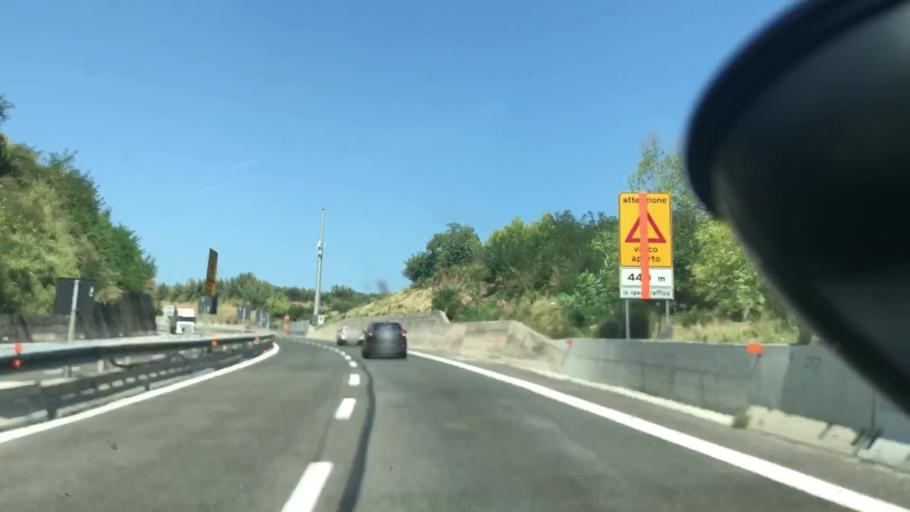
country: IT
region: Abruzzo
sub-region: Provincia di Chieti
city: San Vito Chietino
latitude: 42.2962
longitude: 14.4328
